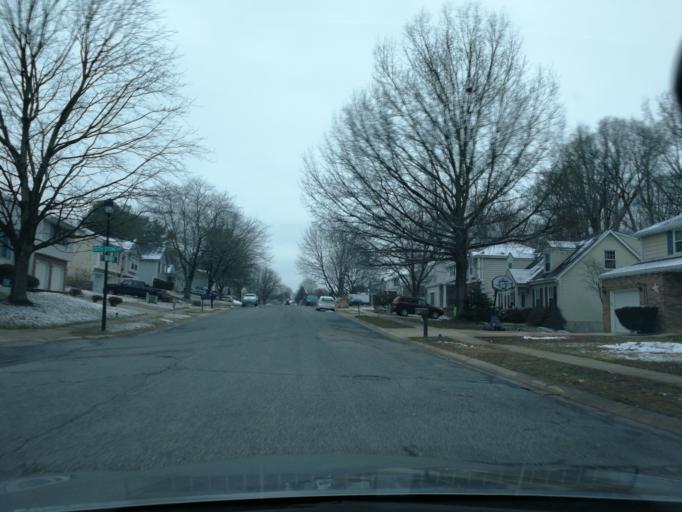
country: US
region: Maryland
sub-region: Harford County
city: Bel Air South
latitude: 39.4859
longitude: -76.3101
